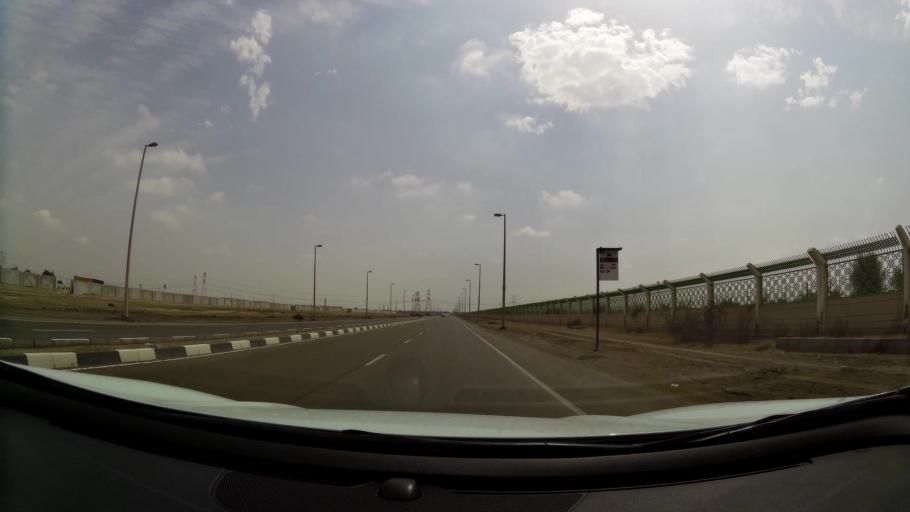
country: AE
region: Abu Dhabi
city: Abu Dhabi
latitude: 24.5305
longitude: 54.6386
